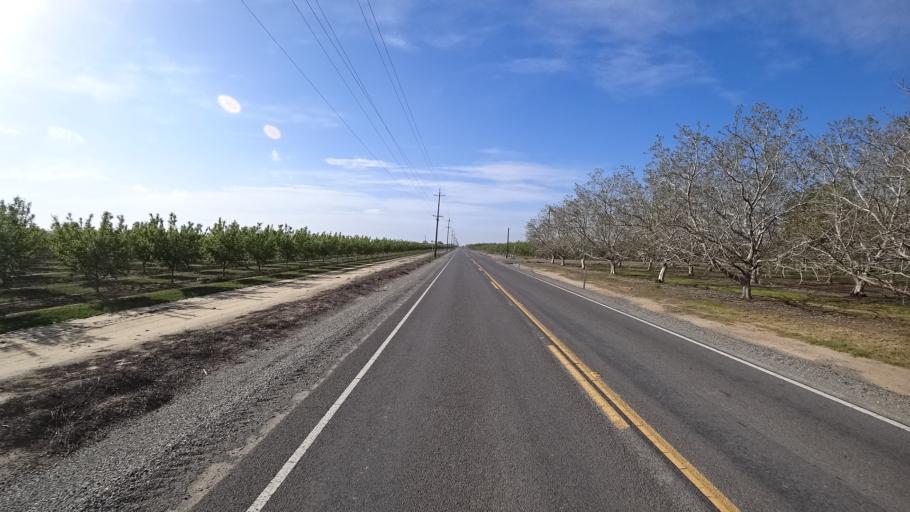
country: US
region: California
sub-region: Glenn County
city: Hamilton City
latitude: 39.6238
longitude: -122.0071
